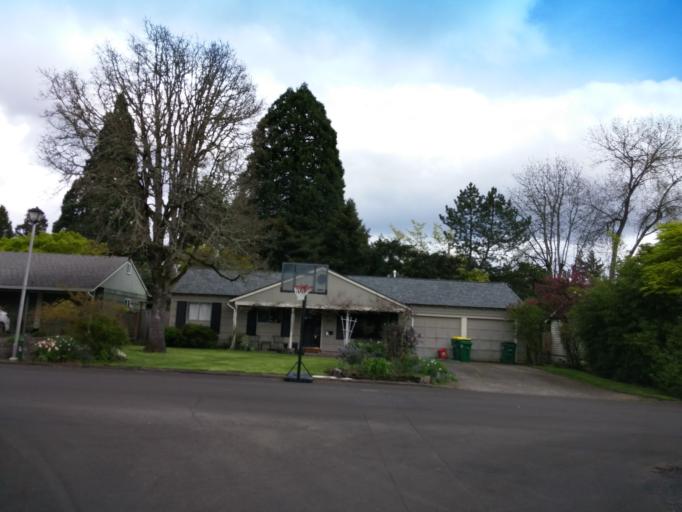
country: US
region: Oregon
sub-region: Washington County
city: Cedar Hills
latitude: 45.5032
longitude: -122.8152
